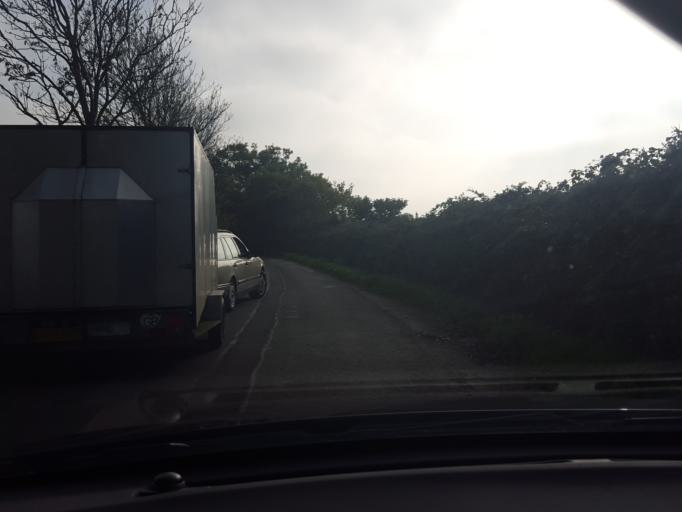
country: GB
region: England
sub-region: Essex
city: Mistley
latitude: 51.9283
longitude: 1.1470
